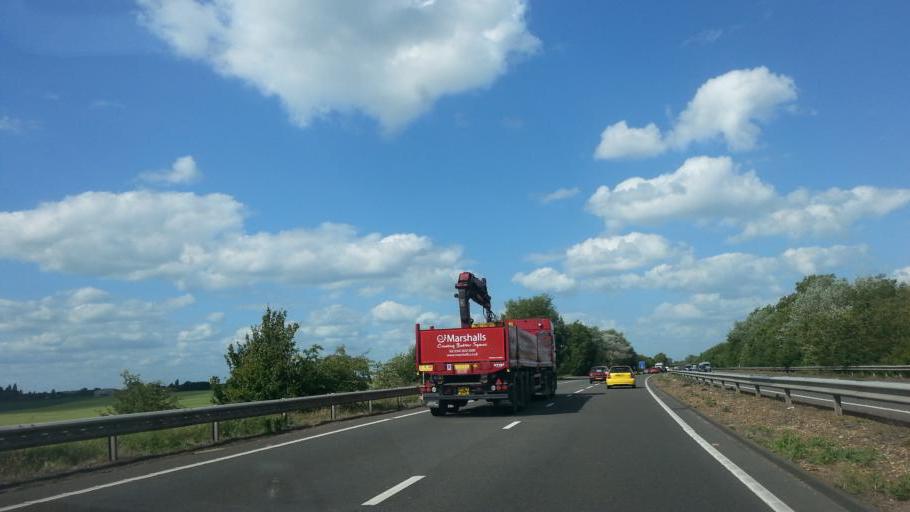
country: GB
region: England
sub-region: Cambridgeshire
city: Eaton Socon
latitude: 52.2296
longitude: -0.2922
